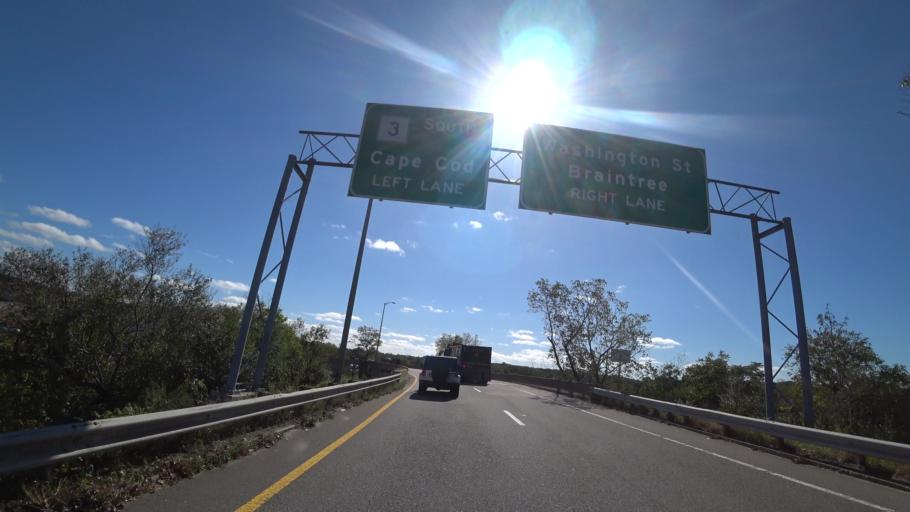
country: US
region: Massachusetts
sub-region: Norfolk County
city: Braintree
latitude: 42.2287
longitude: -71.0108
